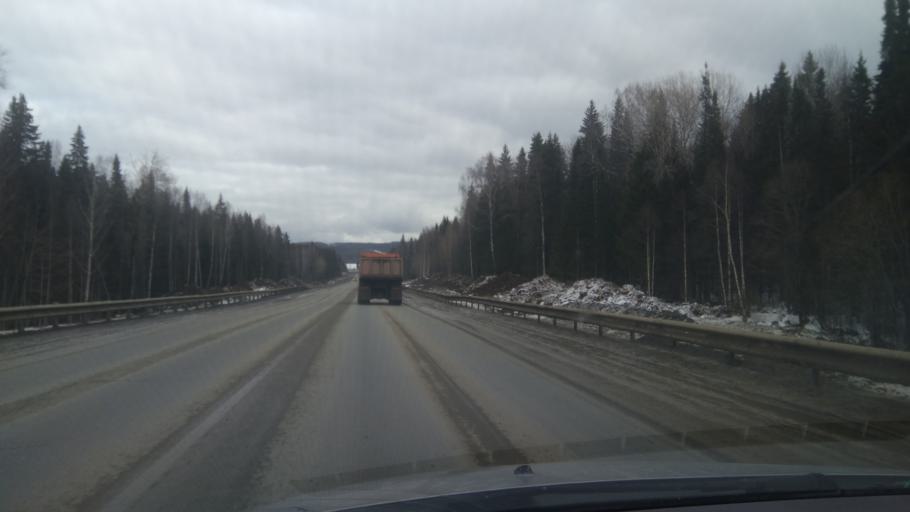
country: RU
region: Sverdlovsk
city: Bisert'
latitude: 56.8291
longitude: 59.1361
